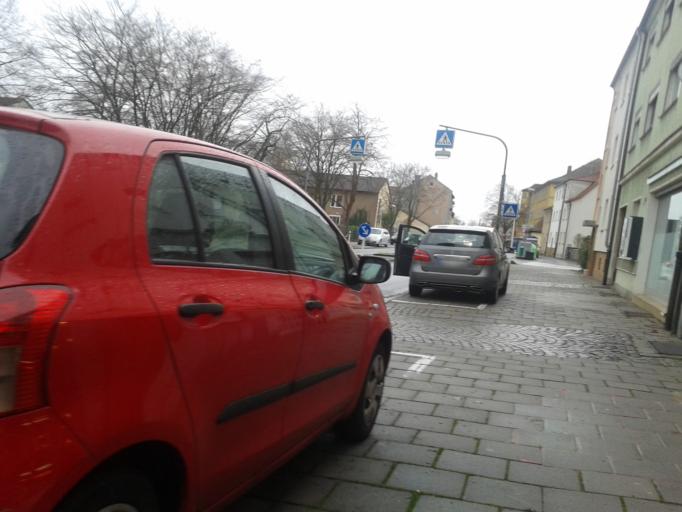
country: DE
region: Bavaria
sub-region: Upper Franconia
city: Bamberg
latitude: 49.9021
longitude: 10.9068
